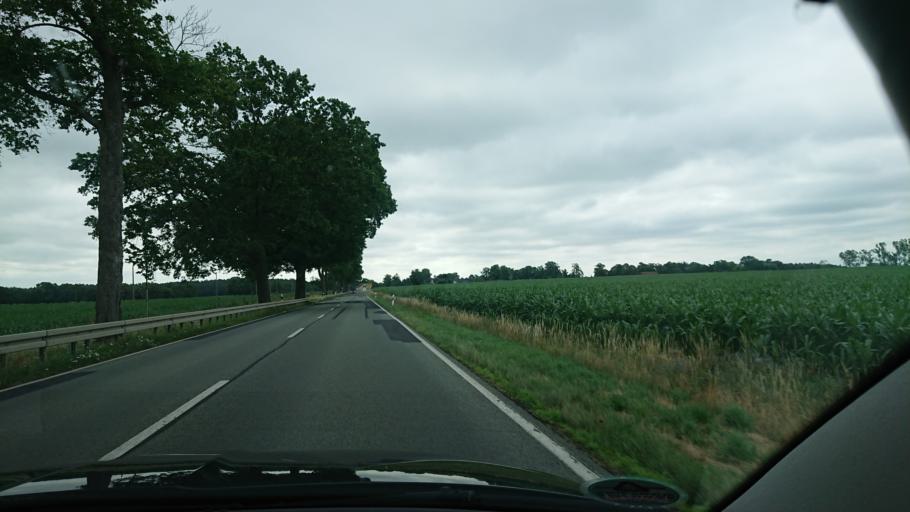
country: DE
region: Brandenburg
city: Plattenburg
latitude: 53.0195
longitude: 11.9997
